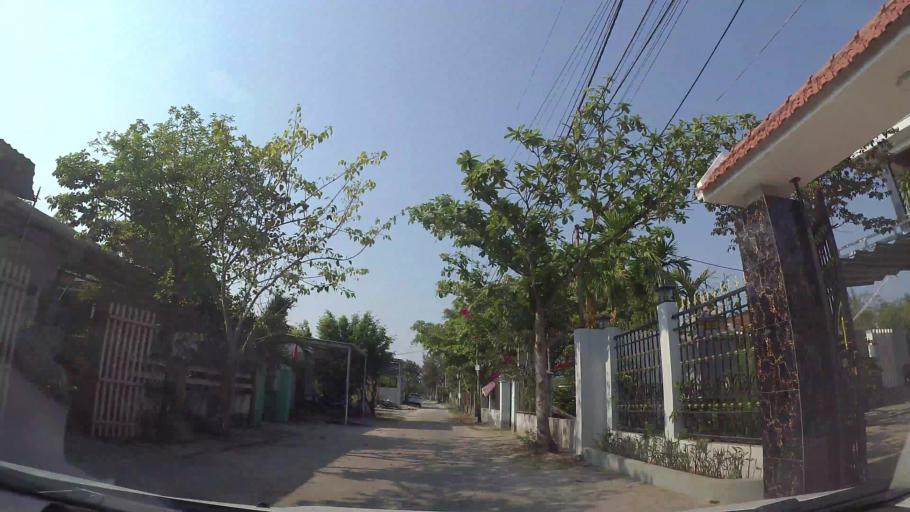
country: VN
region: Quang Nam
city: Quang Nam
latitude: 15.9500
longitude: 108.2672
